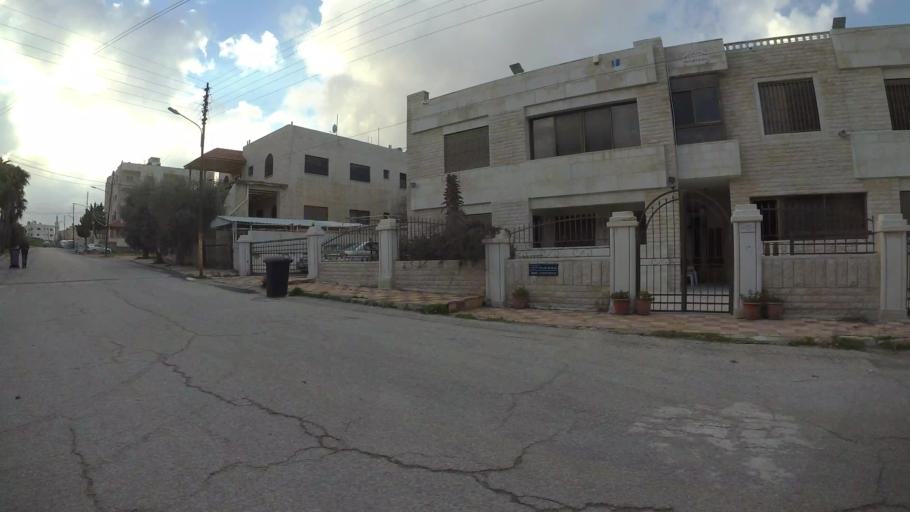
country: JO
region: Amman
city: Al Jubayhah
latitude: 31.9814
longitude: 35.8619
